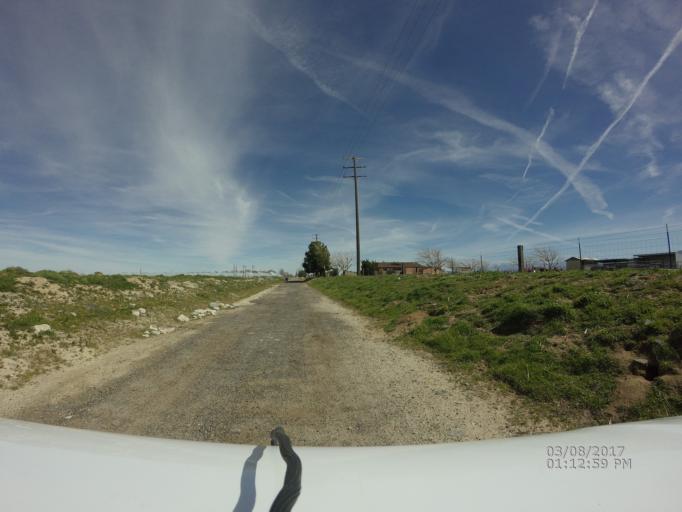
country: US
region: California
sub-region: Los Angeles County
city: Leona Valley
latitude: 34.7184
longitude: -118.2970
